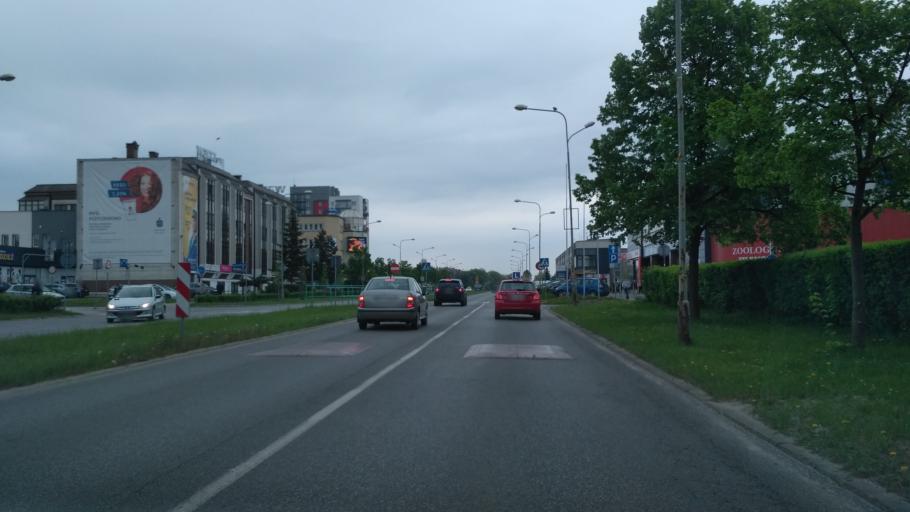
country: PL
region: Lesser Poland Voivodeship
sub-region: Powiat tarnowski
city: Tarnow
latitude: 50.0179
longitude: 20.9991
